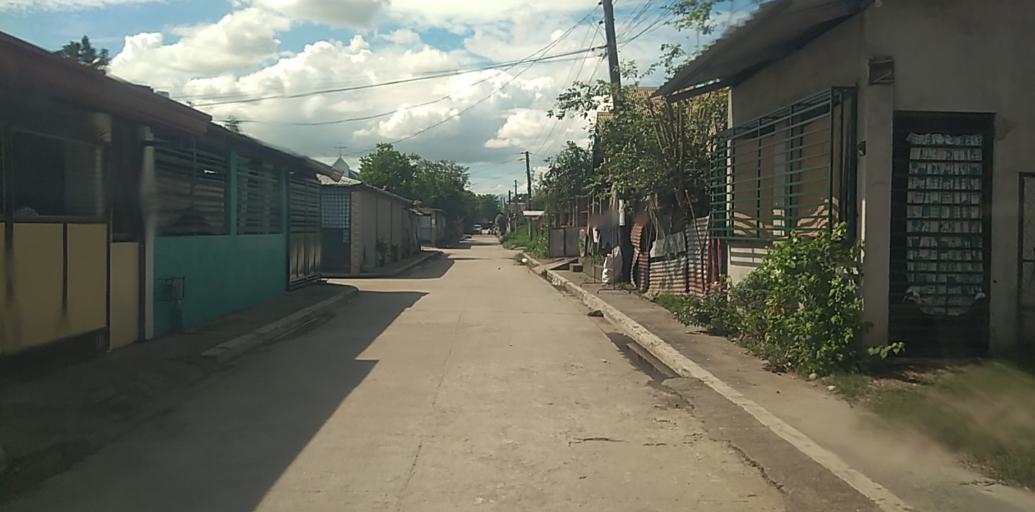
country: PH
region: Central Luzon
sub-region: Province of Pampanga
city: Buensuseso
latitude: 15.1919
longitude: 120.6629
